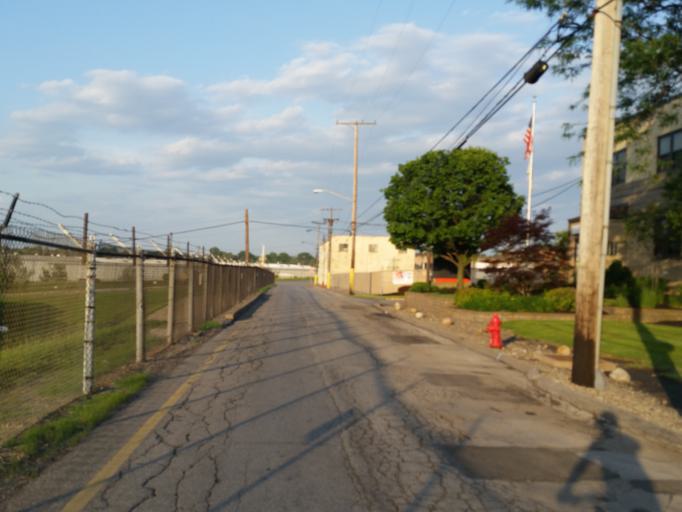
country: US
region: Ohio
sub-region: Cuyahoga County
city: Newburgh Heights
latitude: 41.4640
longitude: -81.6680
